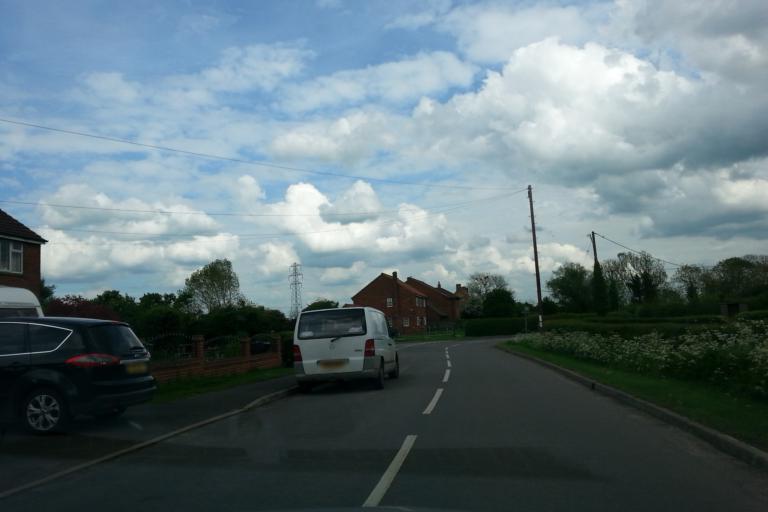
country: GB
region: England
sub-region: Lincolnshire
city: Long Bennington
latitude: 52.9944
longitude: -0.7344
